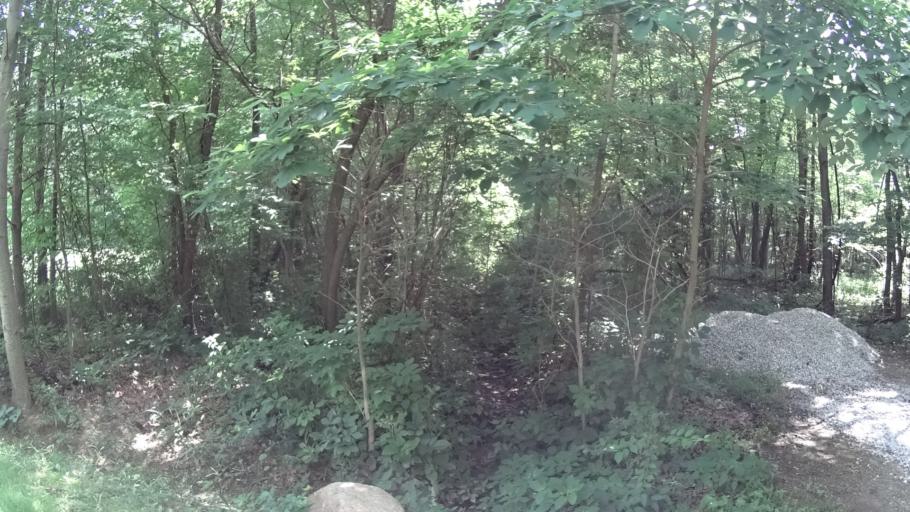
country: US
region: Ohio
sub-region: Lorain County
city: Vermilion
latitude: 41.3878
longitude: -82.3853
